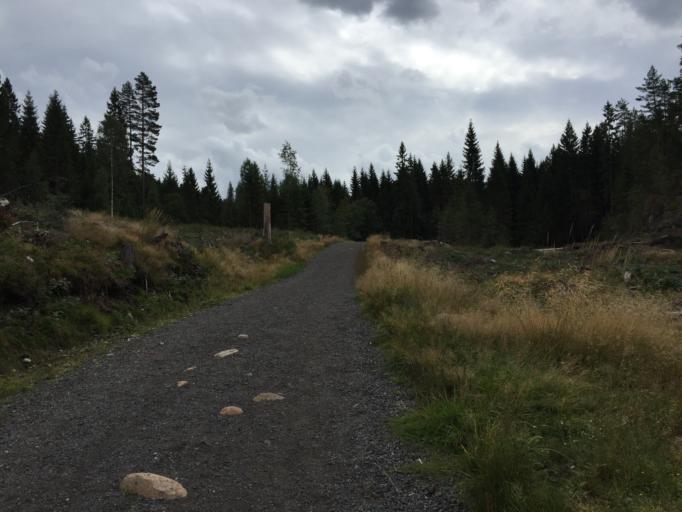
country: NO
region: Akershus
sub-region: Skedsmo
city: Lillestrom
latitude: 59.9178
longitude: 11.0137
